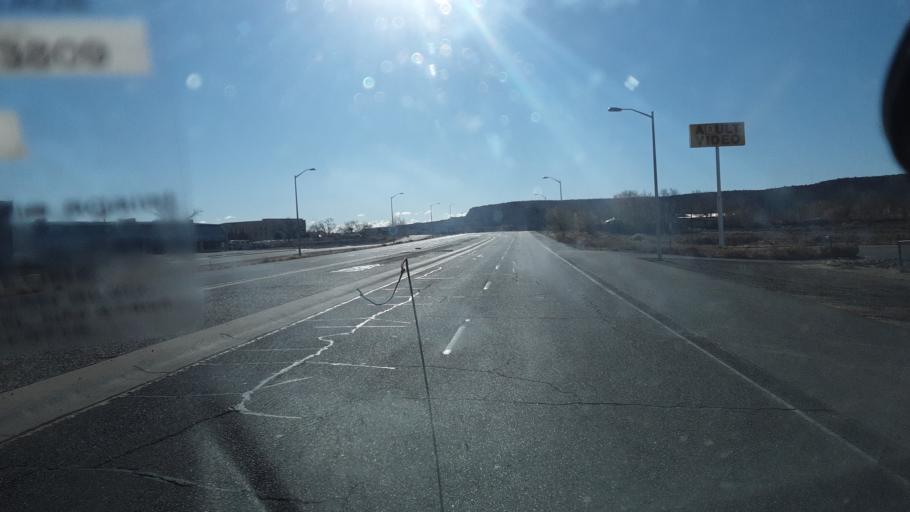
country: US
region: New Mexico
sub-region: San Juan County
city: Farmington
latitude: 36.7243
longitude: -108.1879
